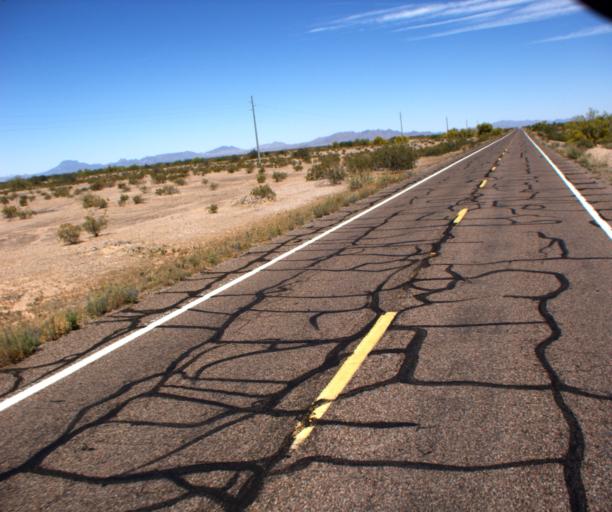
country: US
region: Arizona
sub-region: Maricopa County
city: Gila Bend
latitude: 32.8376
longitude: -112.7786
